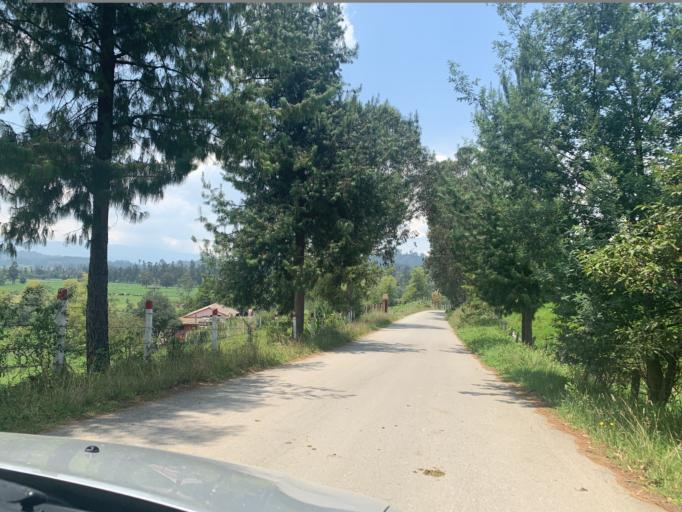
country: CO
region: Boyaca
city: Chiquinquira
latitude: 5.5646
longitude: -73.7506
